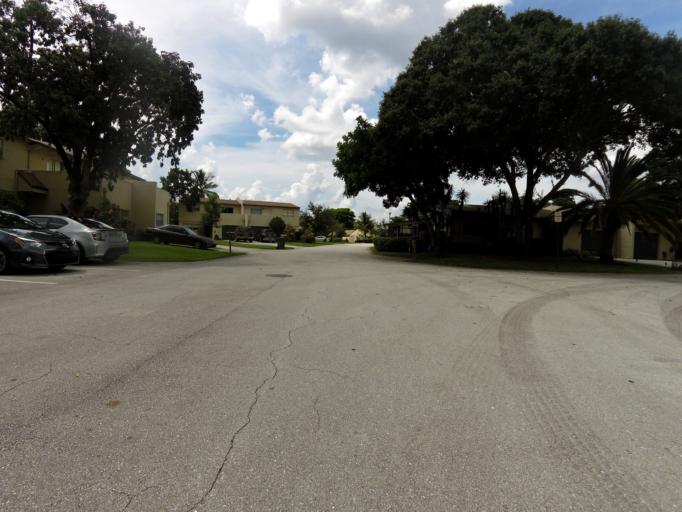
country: US
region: Florida
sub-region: Broward County
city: Cooper City
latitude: 26.0705
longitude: -80.2630
